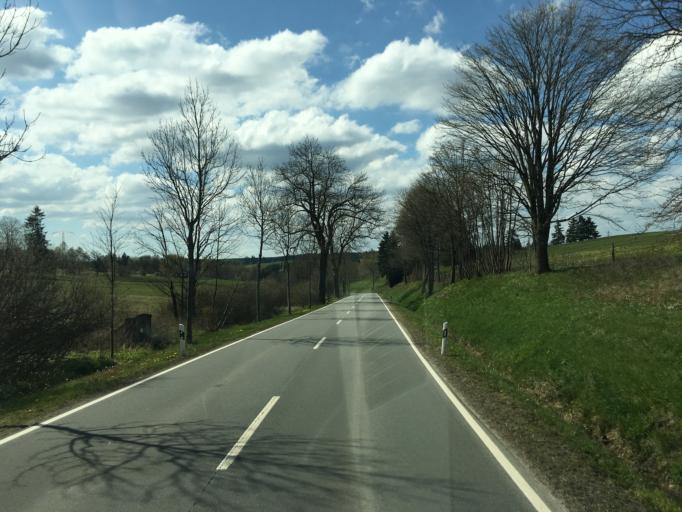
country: DE
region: Saxony-Anhalt
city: Hasselfelde
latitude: 51.6832
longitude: 10.7971
